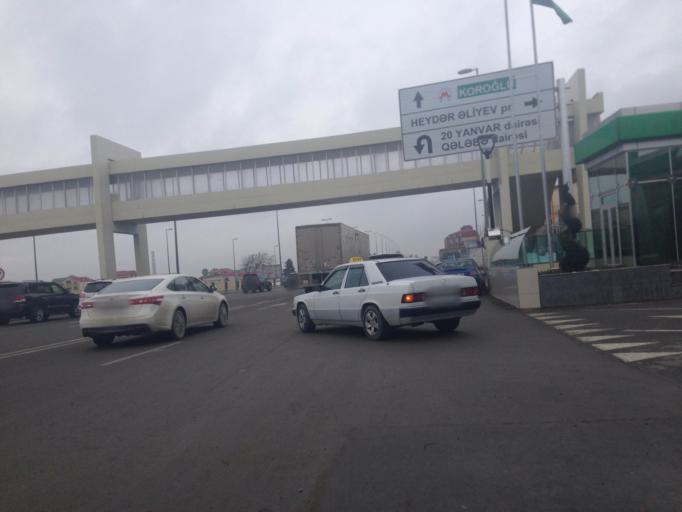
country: AZ
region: Baki
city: Baku
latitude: 40.4180
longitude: 49.8636
